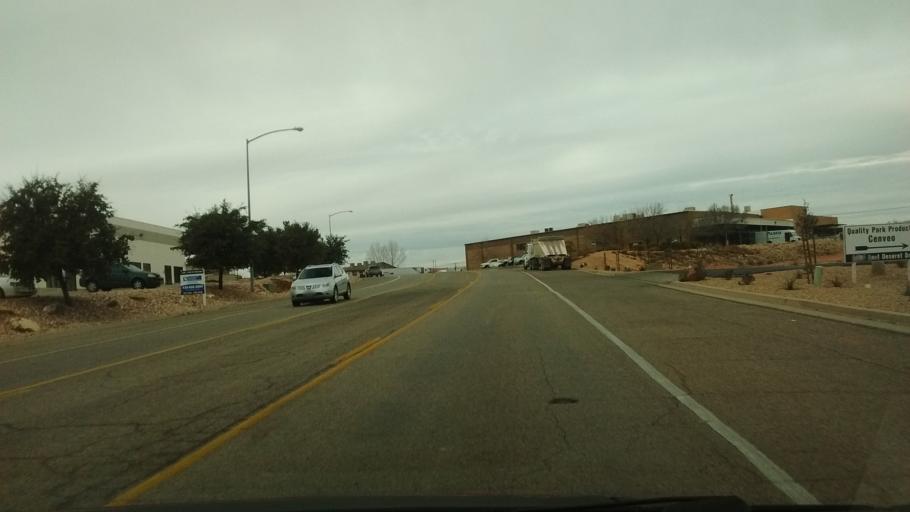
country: US
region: Utah
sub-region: Washington County
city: Washington
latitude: 37.1159
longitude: -113.5158
